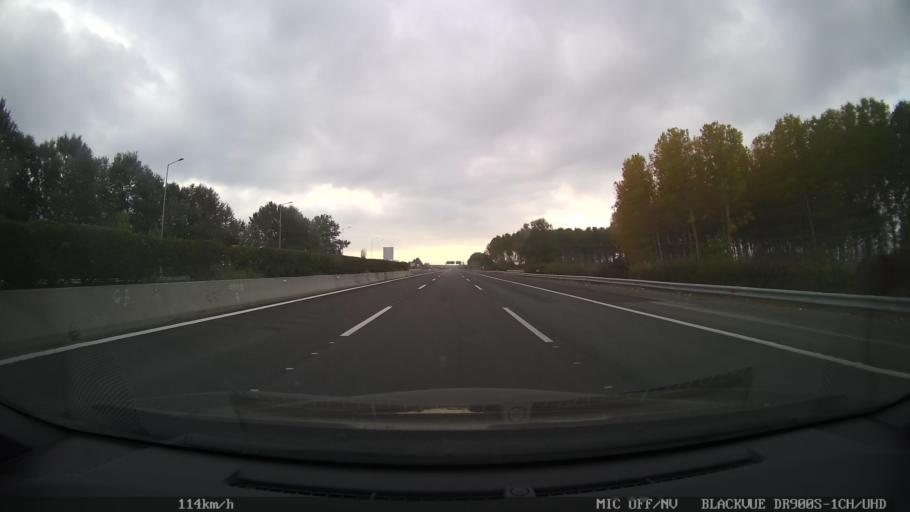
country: GR
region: Central Macedonia
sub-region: Nomos Pierias
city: Nea Efesos
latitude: 40.2021
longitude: 22.5466
